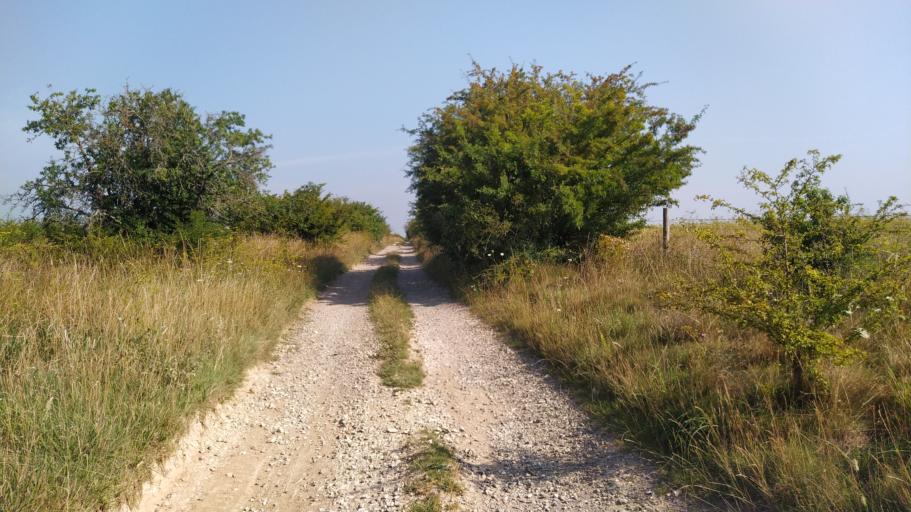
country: GB
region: England
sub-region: Wiltshire
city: Shrewton
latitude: 51.1711
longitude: -1.9521
